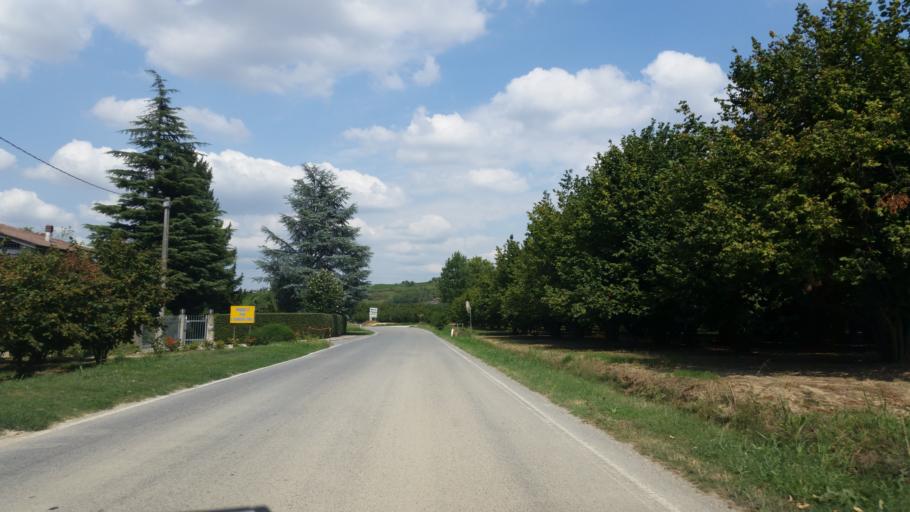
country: IT
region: Piedmont
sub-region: Provincia di Cuneo
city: Neive-Borgonovo
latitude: 44.7130
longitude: 8.1149
